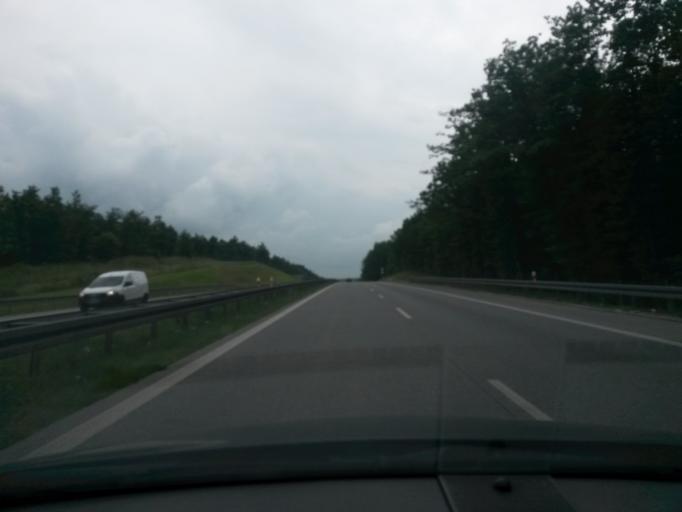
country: PL
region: Lodz Voivodeship
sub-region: Powiat skierniewicki
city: Kowiesy
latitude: 51.8352
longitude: 20.3404
